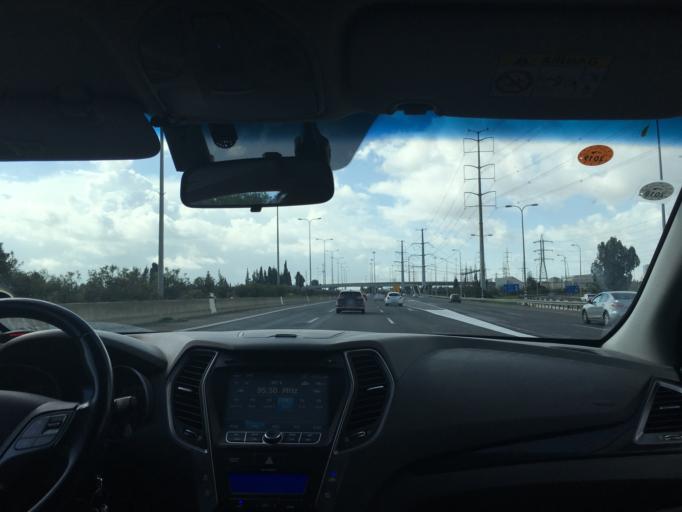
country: IL
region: Tel Aviv
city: Azor
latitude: 32.0249
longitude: 34.8259
